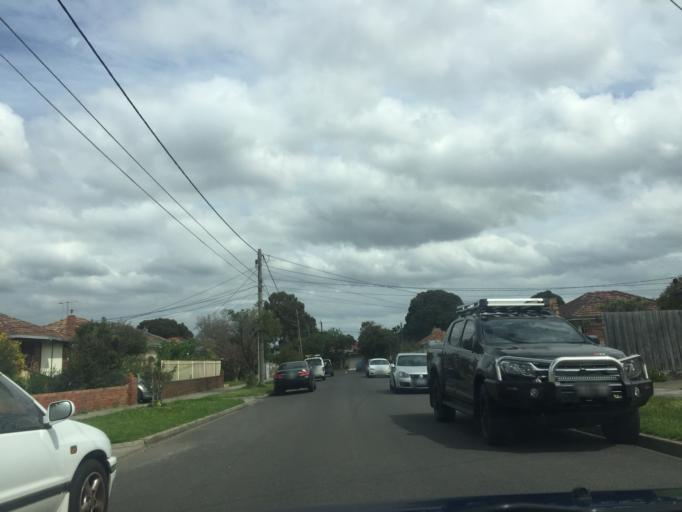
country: AU
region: Victoria
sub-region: Darebin
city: Preston
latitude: -37.7429
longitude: 145.0143
